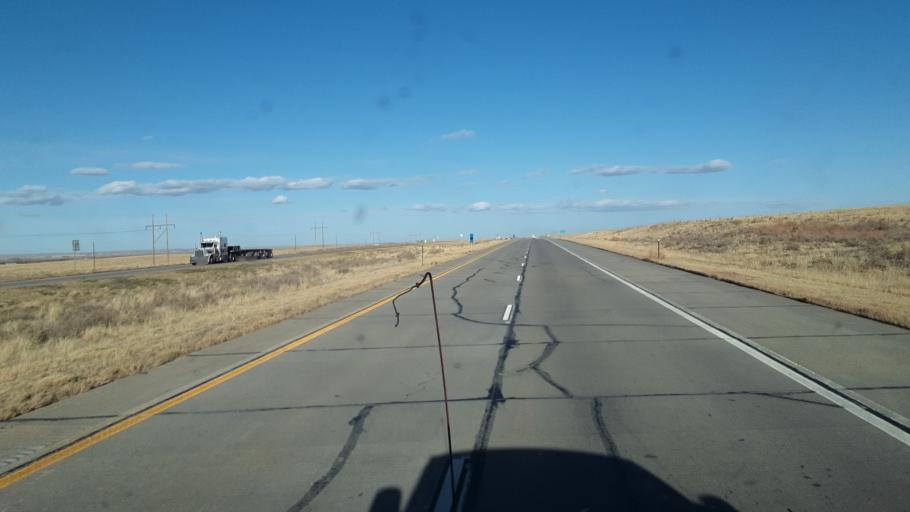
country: US
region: Colorado
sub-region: Logan County
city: Sterling
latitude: 40.7023
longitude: -103.0658
